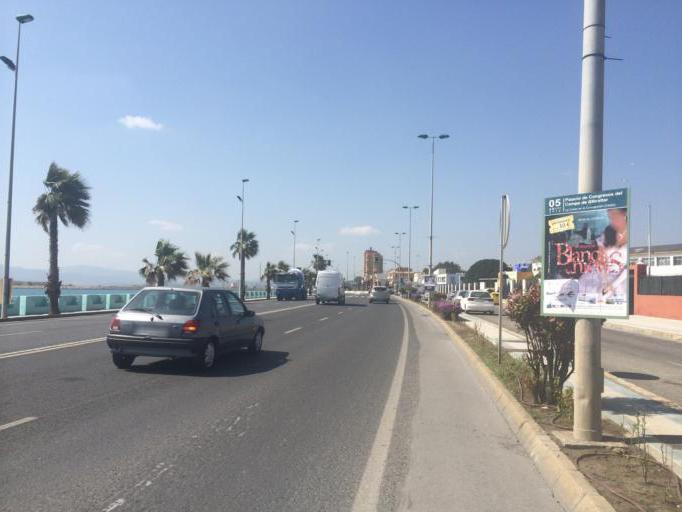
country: ES
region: Andalusia
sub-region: Provincia de Cadiz
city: La Linea de la Concepcion
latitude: 36.1660
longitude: -5.3626
